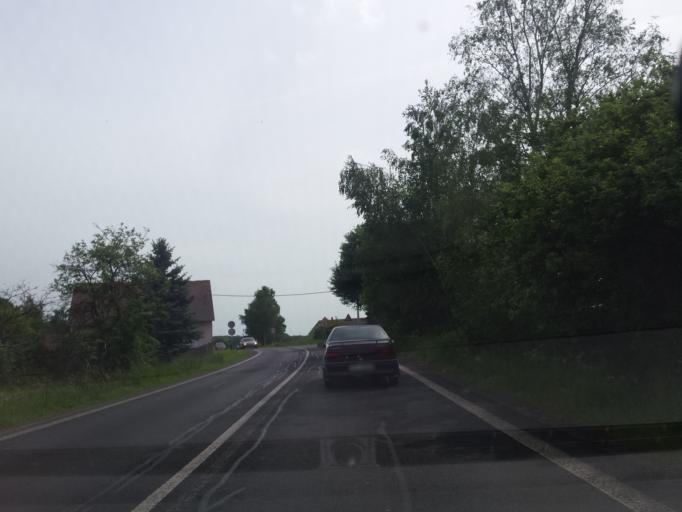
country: CZ
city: Novy Bor
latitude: 50.7326
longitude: 14.5470
